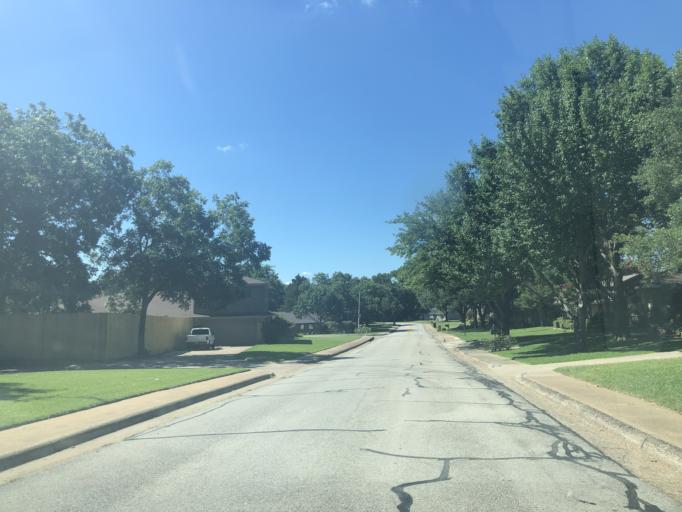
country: US
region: Texas
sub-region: Dallas County
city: Duncanville
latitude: 32.6372
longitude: -96.9301
